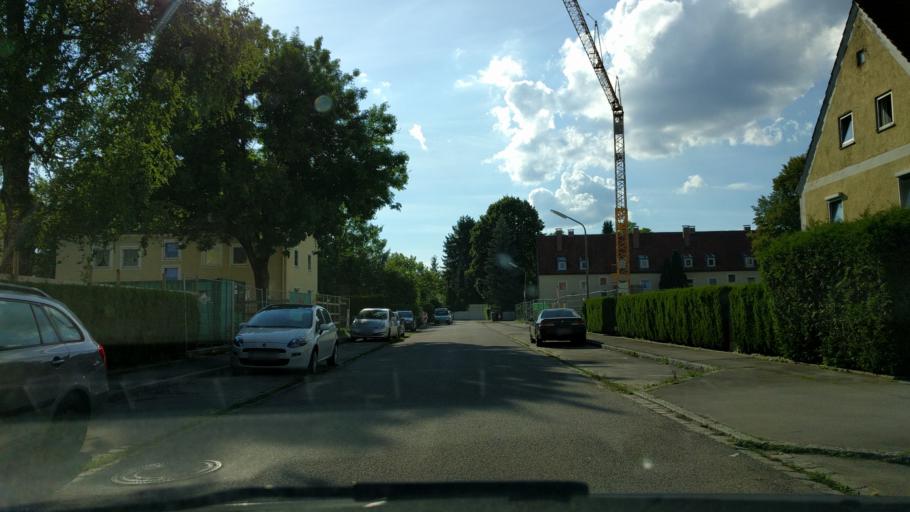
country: DE
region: Bavaria
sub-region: Upper Bavaria
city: Grunwald
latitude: 48.0385
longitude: 11.5344
